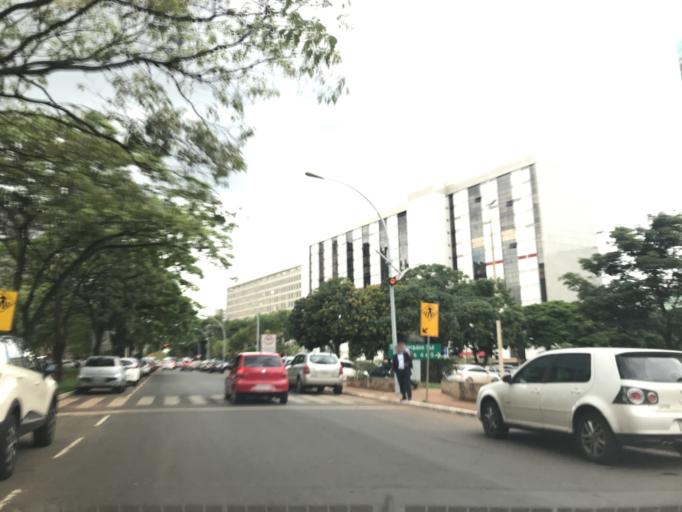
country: BR
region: Federal District
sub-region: Brasilia
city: Brasilia
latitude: -15.8038
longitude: -47.8831
